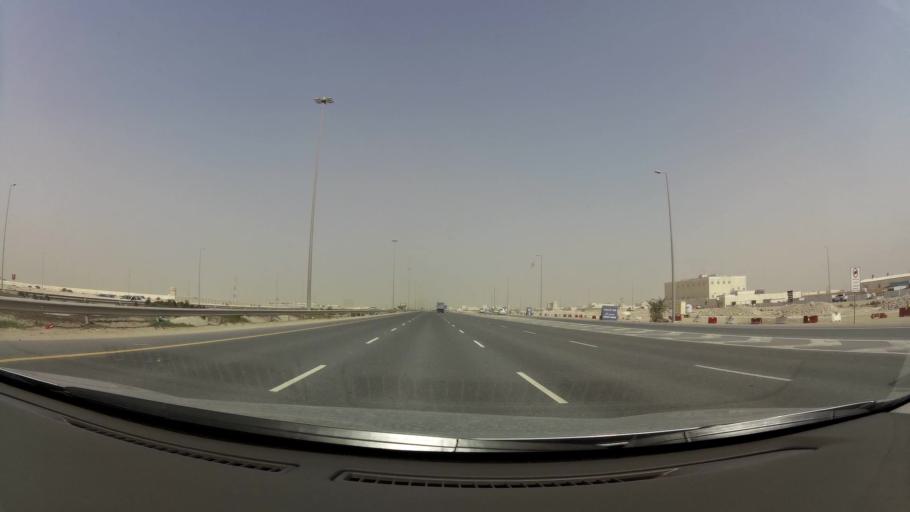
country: QA
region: Baladiyat ar Rayyan
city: Ar Rayyan
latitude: 25.1807
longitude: 51.3497
